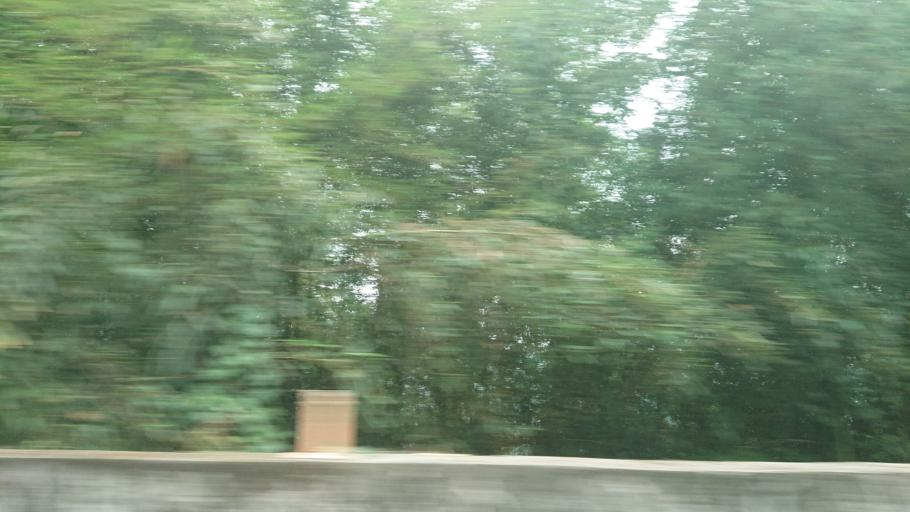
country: TW
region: Taiwan
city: Lugu
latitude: 23.6052
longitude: 120.7085
